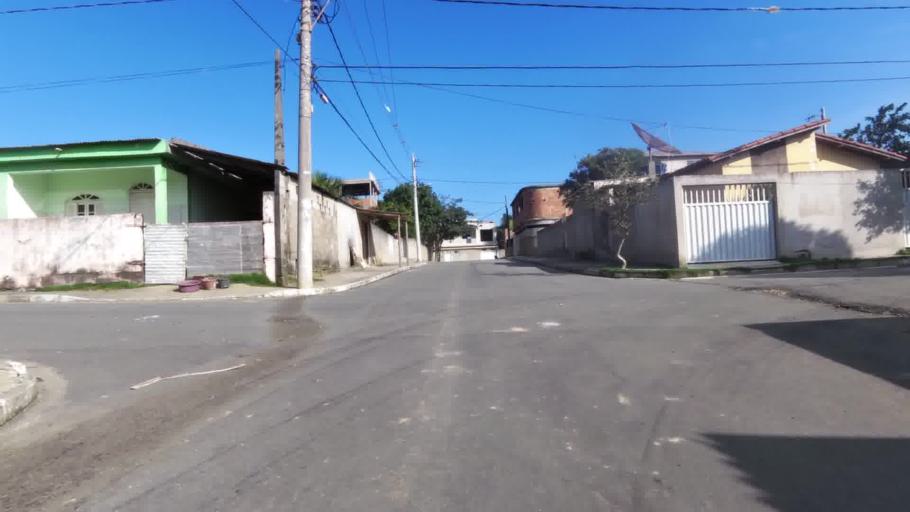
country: BR
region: Espirito Santo
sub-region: Piuma
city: Piuma
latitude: -20.8174
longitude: -40.6232
